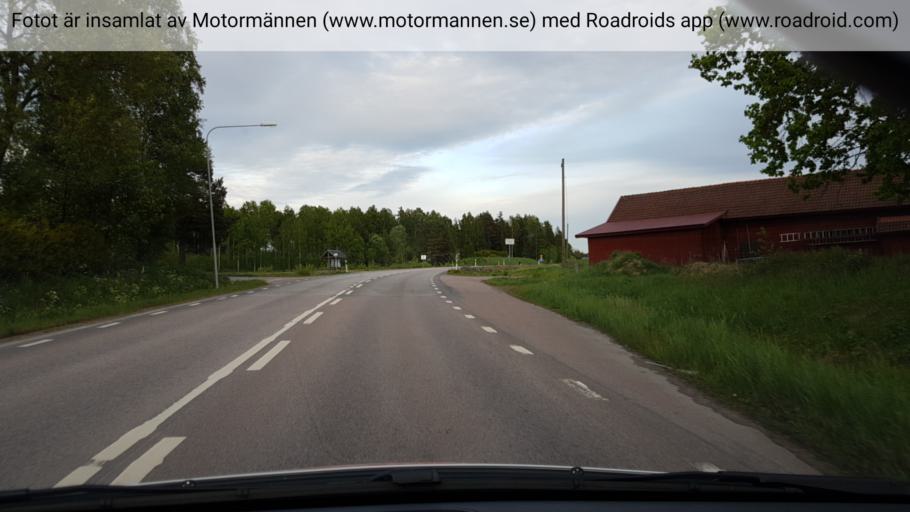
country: SE
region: Vaestmanland
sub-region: Kopings Kommun
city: Kolsva
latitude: 59.5868
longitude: 15.8632
